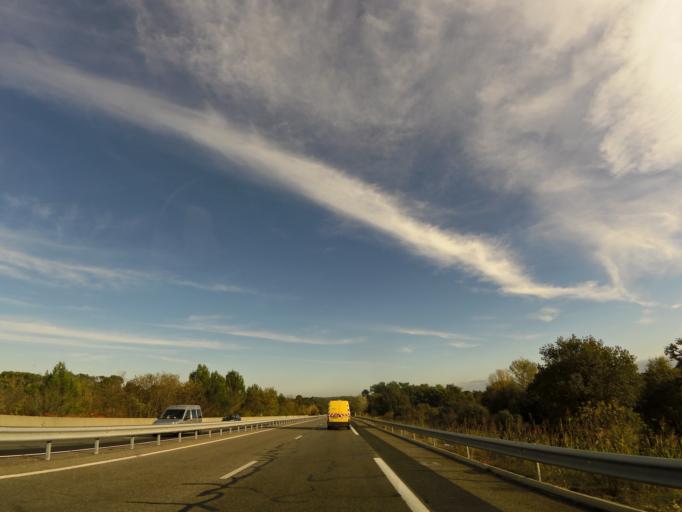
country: FR
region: Languedoc-Roussillon
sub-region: Departement du Gard
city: Vezenobres
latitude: 44.0439
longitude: 4.1340
